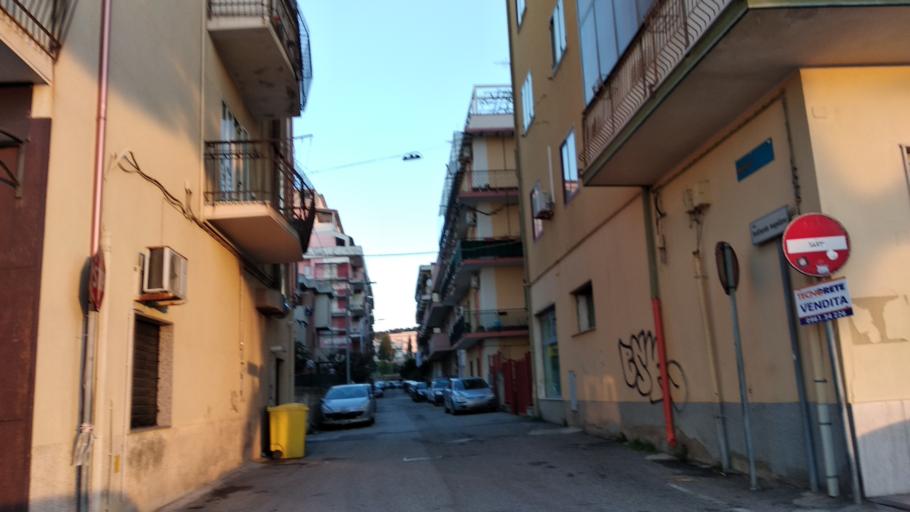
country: IT
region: Calabria
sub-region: Provincia di Catanzaro
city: Barone
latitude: 38.8268
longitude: 16.6264
